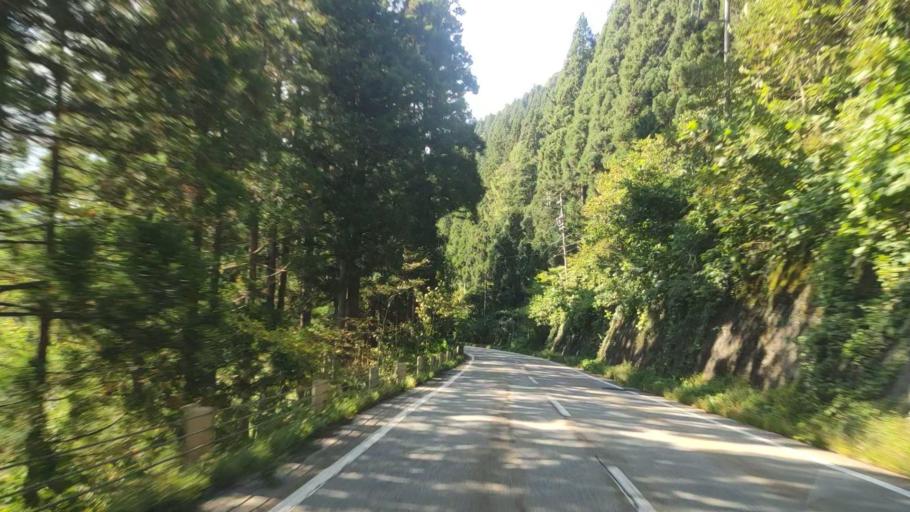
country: JP
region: Gifu
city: Takayama
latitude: 36.2963
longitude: 137.1290
